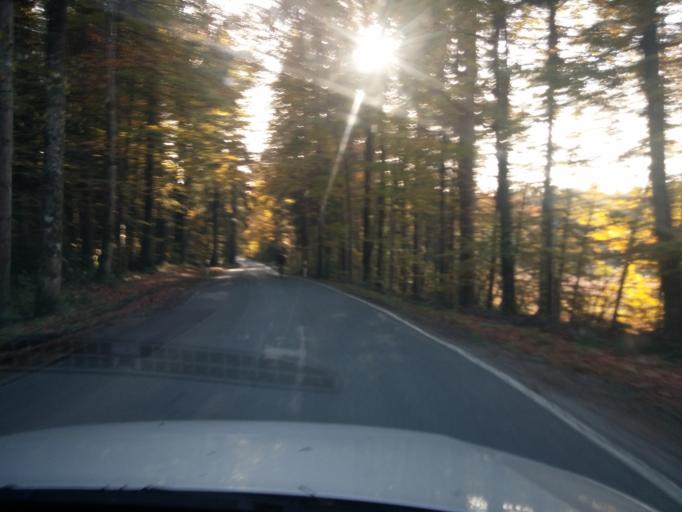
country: DE
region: Bavaria
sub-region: Upper Bavaria
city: Dietramszell
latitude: 47.8146
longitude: 11.5795
